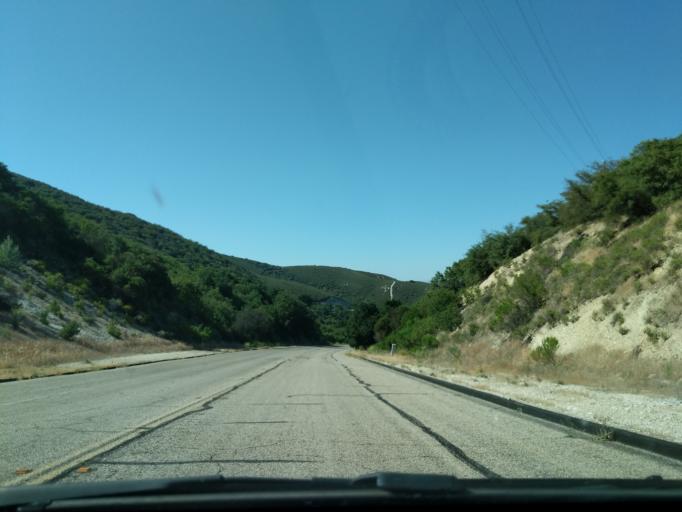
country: US
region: California
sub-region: Monterey County
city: King City
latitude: 36.0778
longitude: -121.1784
